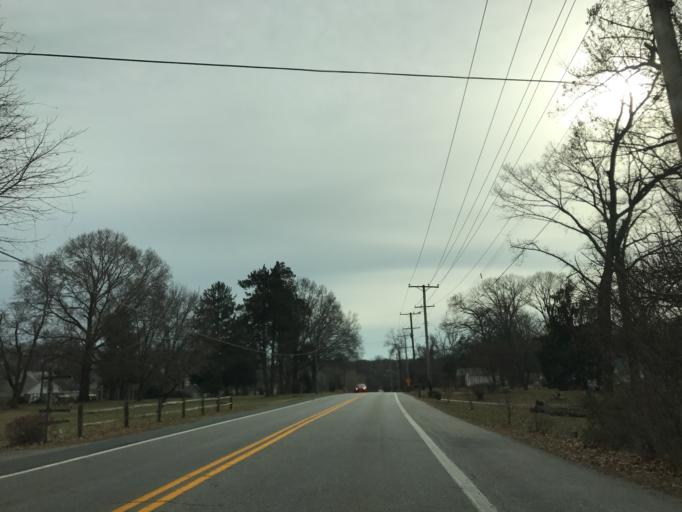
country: US
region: Maryland
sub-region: Anne Arundel County
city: Pasadena
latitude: 39.1179
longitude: -76.5608
